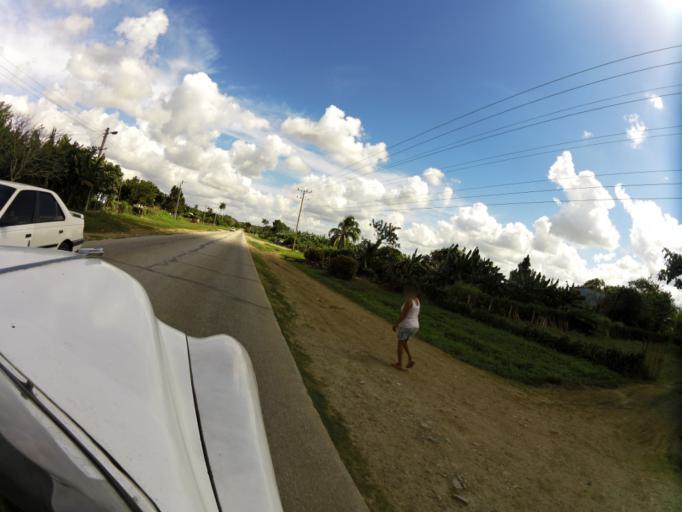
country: CU
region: Holguin
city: Cacocum
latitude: 20.8578
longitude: -76.4576
